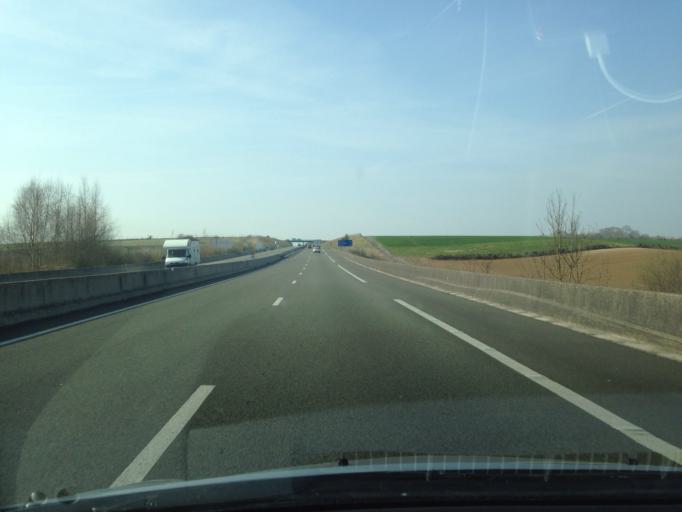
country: FR
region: Picardie
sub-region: Departement de la Somme
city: Sailly-Flibeaucourt
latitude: 50.1446
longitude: 1.8030
